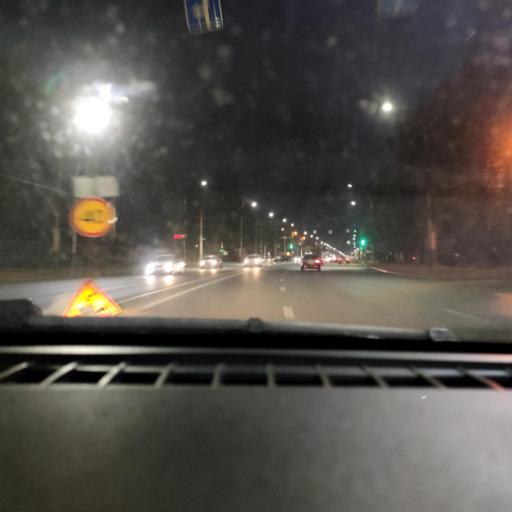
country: RU
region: Voronezj
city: Voronezh
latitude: 51.7022
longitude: 39.2749
